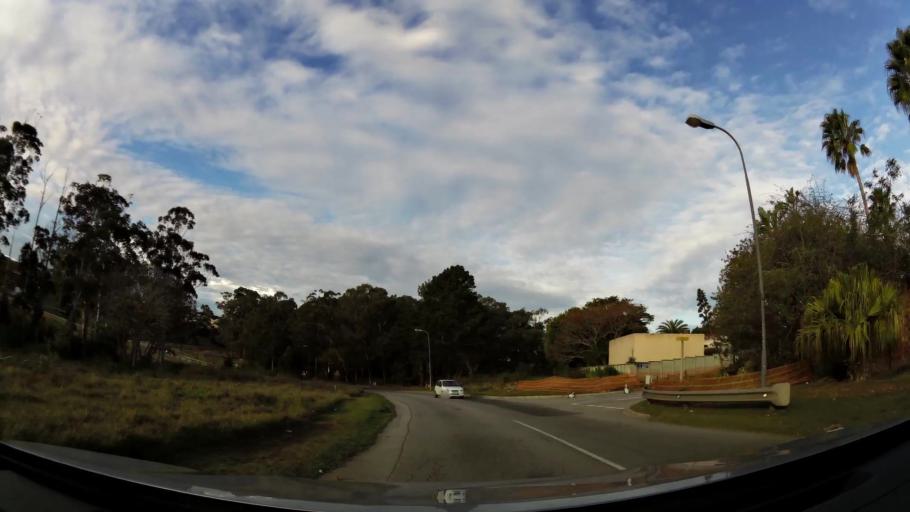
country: ZA
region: Eastern Cape
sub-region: Nelson Mandela Bay Metropolitan Municipality
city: Port Elizabeth
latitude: -33.9543
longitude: 25.5067
